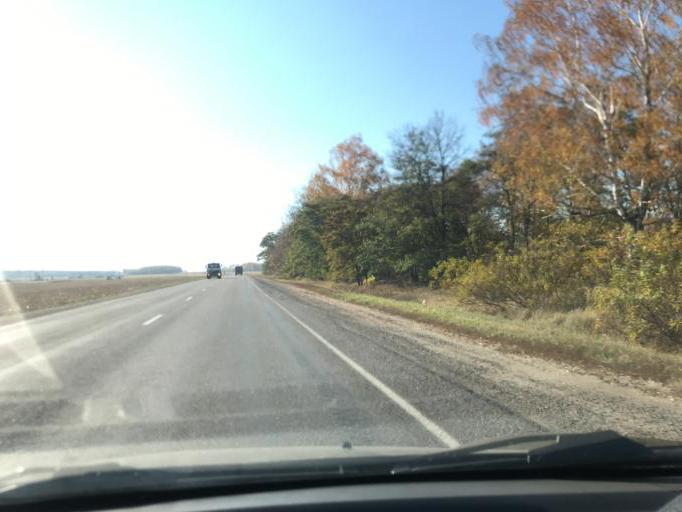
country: BY
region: Gomel
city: Rechytsa
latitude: 52.2653
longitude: 30.2511
